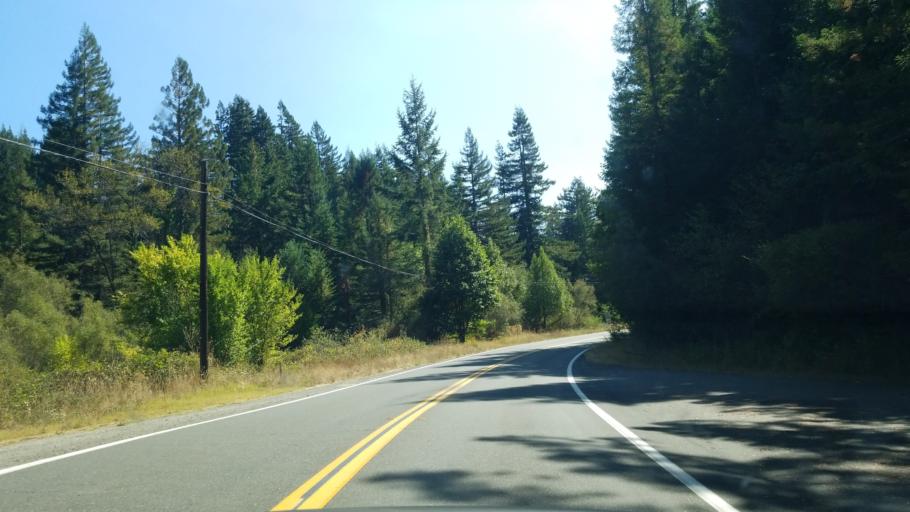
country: US
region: California
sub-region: Humboldt County
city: Redway
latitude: 40.3275
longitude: -123.9256
